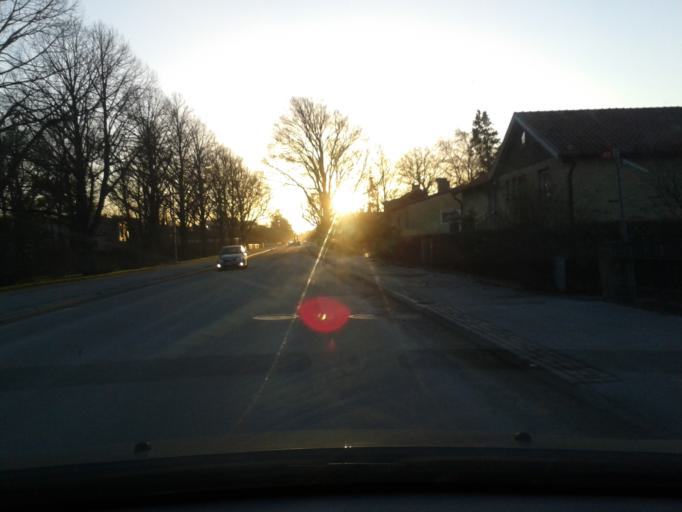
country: SE
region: Gotland
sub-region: Gotland
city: Visby
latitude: 57.6282
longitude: 18.2843
